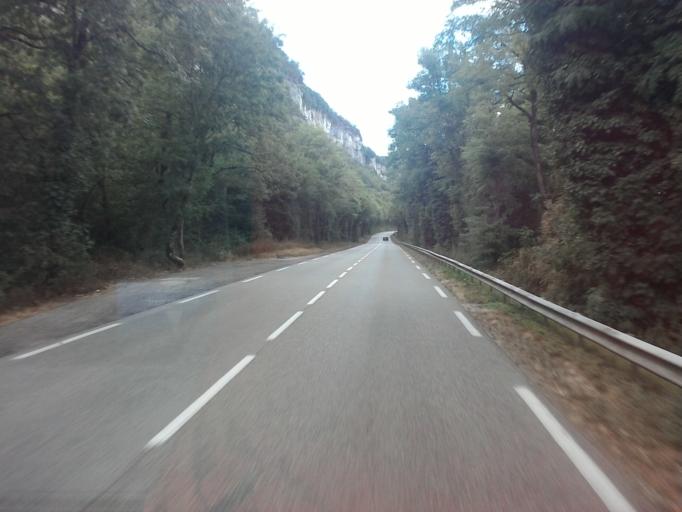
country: FR
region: Rhone-Alpes
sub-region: Departement de l'Ain
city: Sault-Brenaz
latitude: 45.8604
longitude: 5.3898
